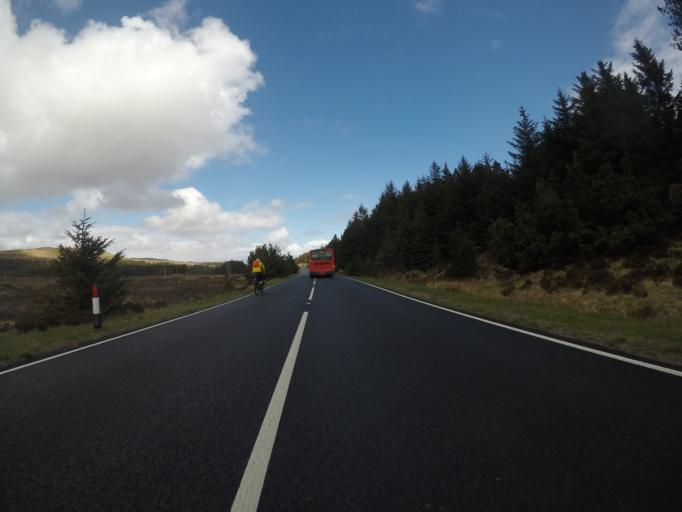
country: GB
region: Scotland
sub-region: Highland
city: Isle of Skye
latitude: 57.3238
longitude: -6.2046
